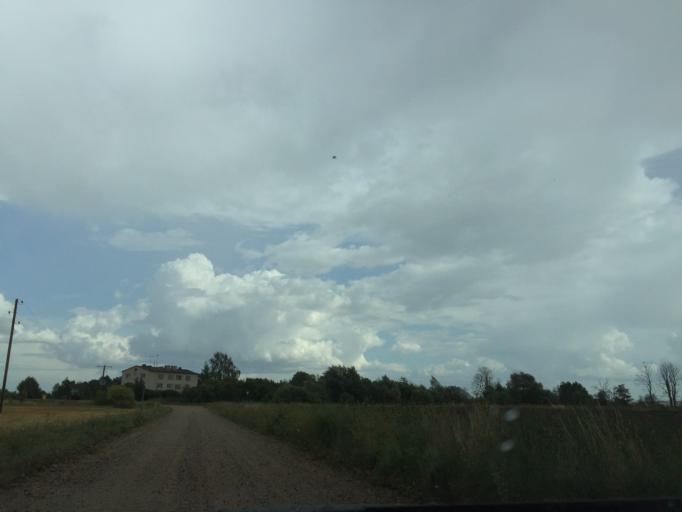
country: LV
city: Tervete
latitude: 56.3665
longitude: 23.4867
